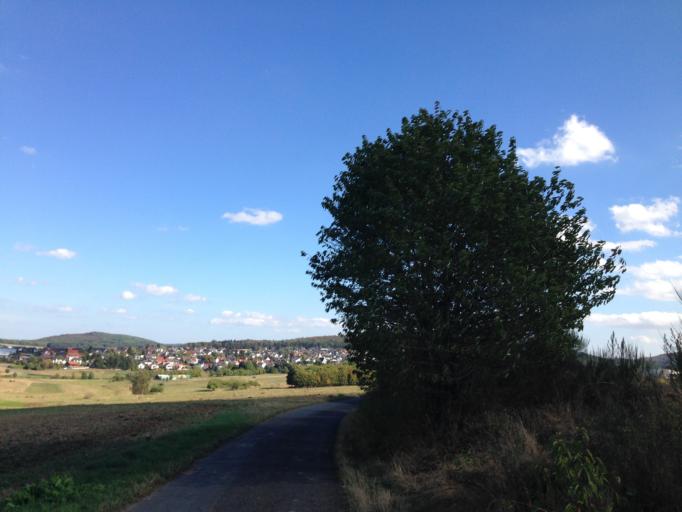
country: DE
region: Hesse
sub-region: Regierungsbezirk Giessen
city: Bischoffen
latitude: 50.6768
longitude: 8.5082
